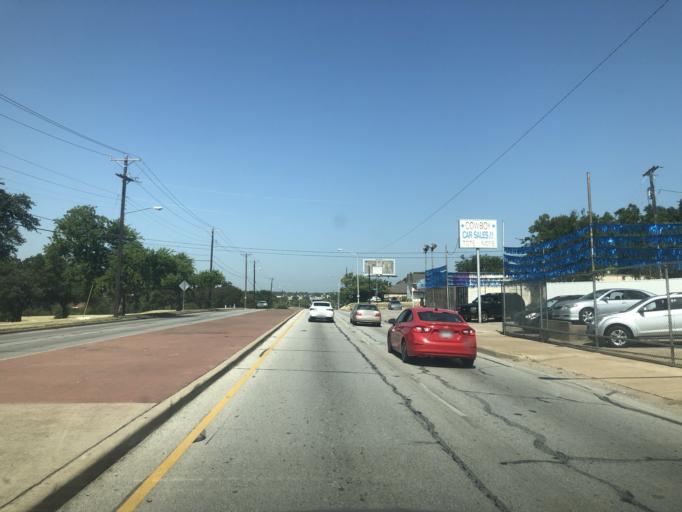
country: US
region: Texas
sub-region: Tarrant County
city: Blue Mound
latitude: 32.7953
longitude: -97.3326
